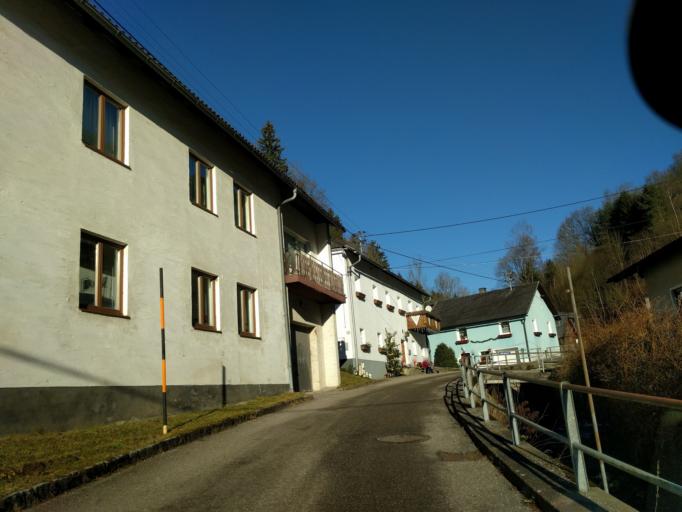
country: AT
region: Upper Austria
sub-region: Politischer Bezirk Urfahr-Umgebung
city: Kirchschlag bei Linz
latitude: 48.4038
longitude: 14.2962
